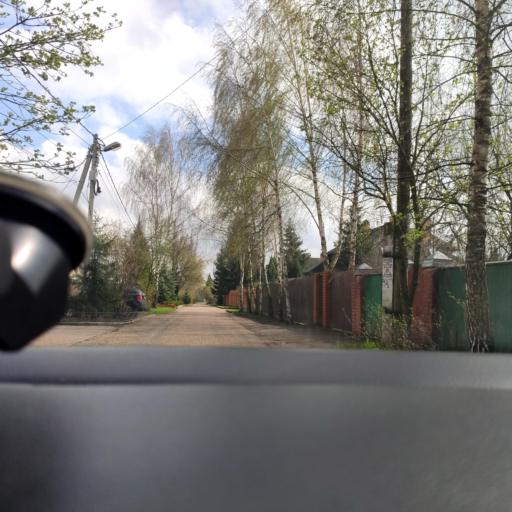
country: RU
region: Moskovskaya
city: Nikolina Gora
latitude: 55.7358
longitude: 36.9822
